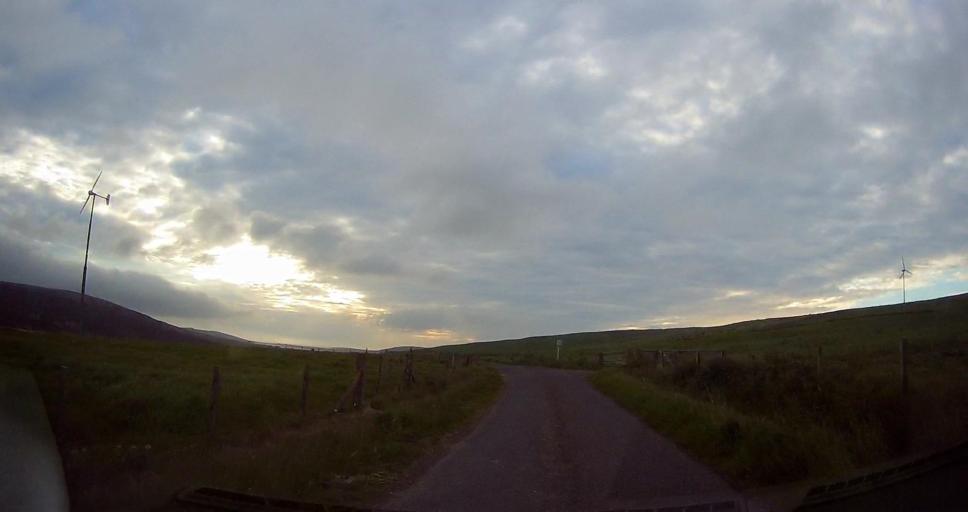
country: GB
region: Scotland
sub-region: Orkney Islands
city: Stromness
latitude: 59.0959
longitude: -3.1905
